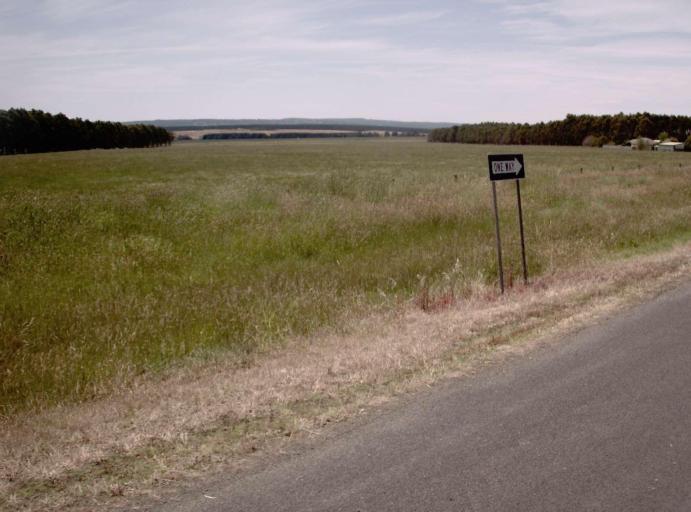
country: AU
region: Victoria
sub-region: Latrobe
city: Morwell
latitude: -38.2266
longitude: 146.4627
